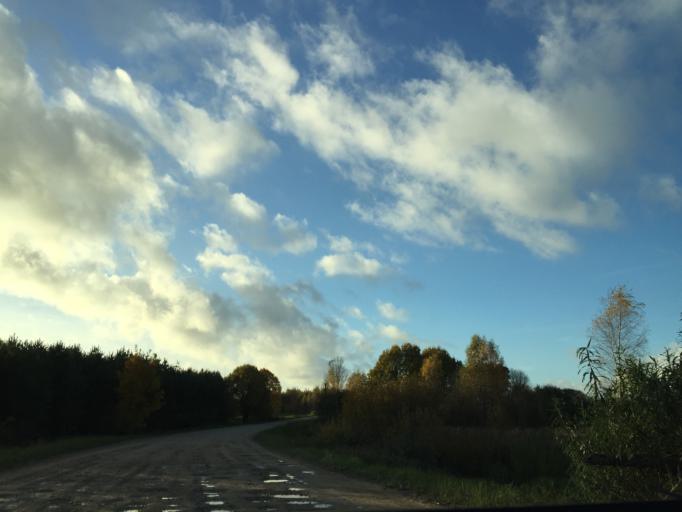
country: LV
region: Ogre
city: Jumprava
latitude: 56.7995
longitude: 25.0344
